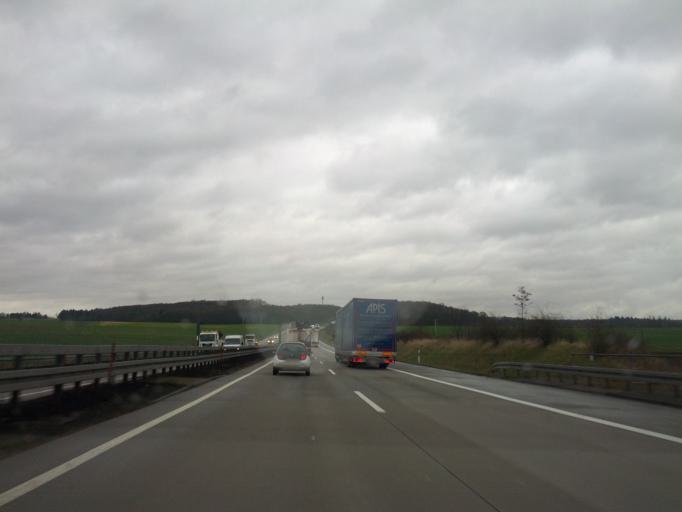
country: DE
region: Hesse
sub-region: Regierungsbezirk Darmstadt
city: Munzenberg
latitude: 50.4999
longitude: 8.7404
